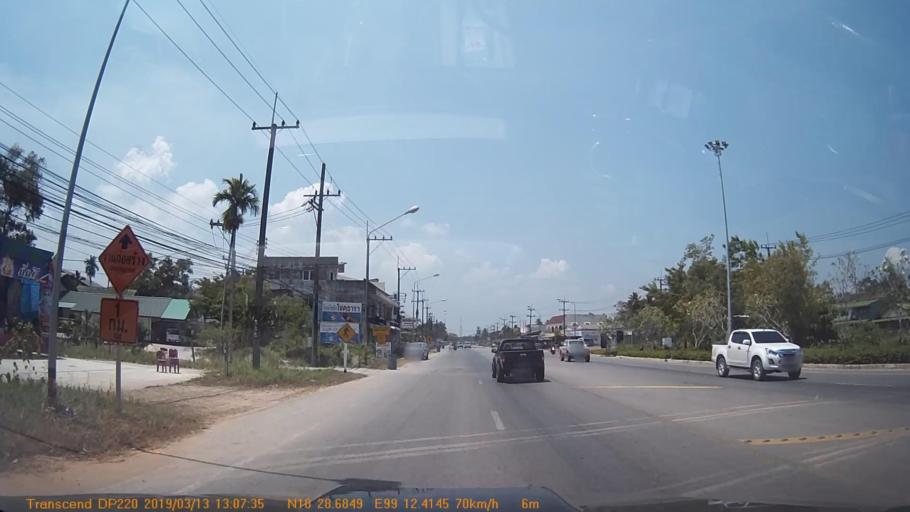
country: TH
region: Chumphon
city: Chumphon
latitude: 10.4783
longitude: 99.2066
